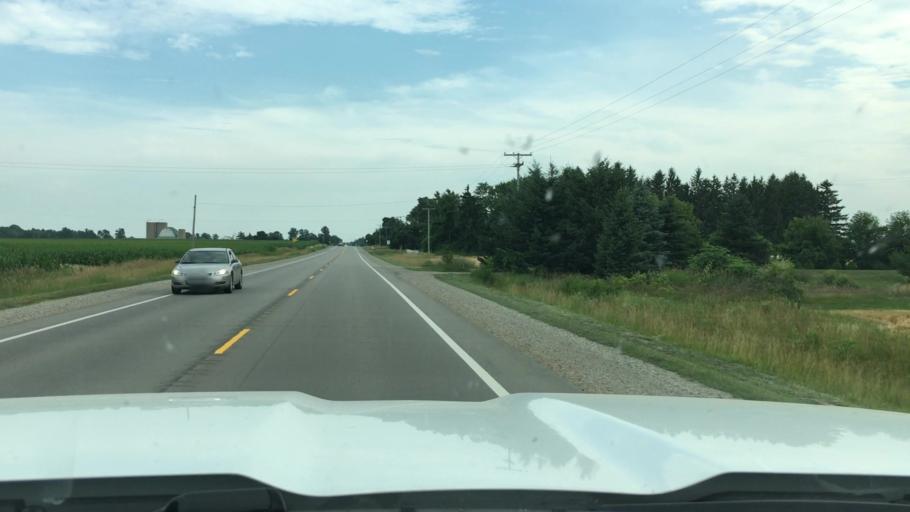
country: US
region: Michigan
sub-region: Sanilac County
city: Marlette
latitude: 43.3662
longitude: -83.0854
